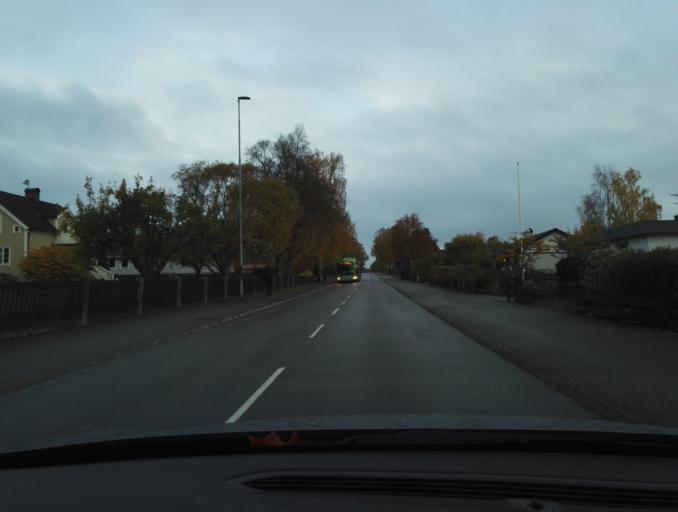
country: SE
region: Kronoberg
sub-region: Vaxjo Kommun
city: Vaexjoe
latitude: 56.9083
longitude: 14.7394
